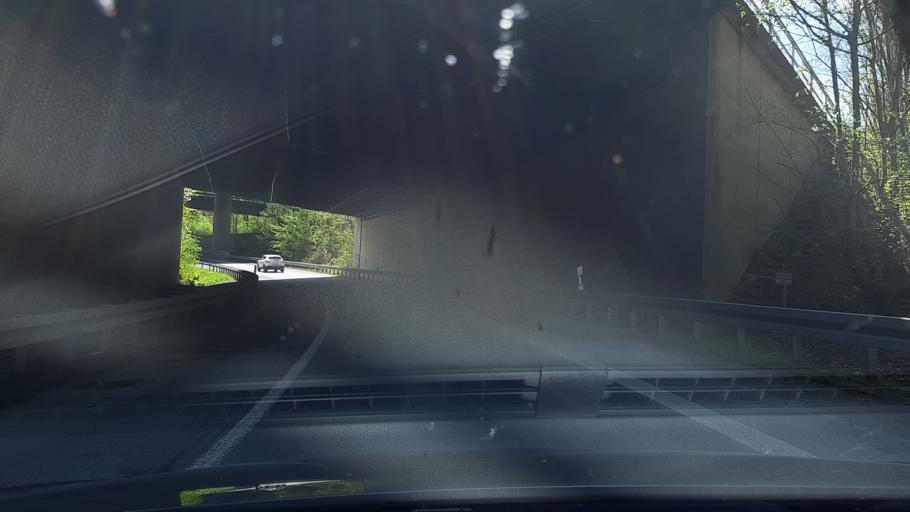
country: DE
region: Hesse
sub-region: Regierungsbezirk Giessen
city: Asslar
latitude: 50.5972
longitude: 8.4889
